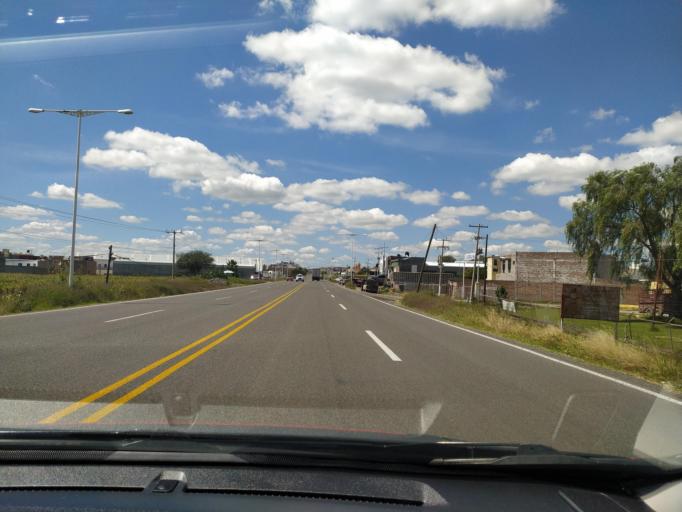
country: MX
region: Jalisco
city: San Miguel el Alto
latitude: 21.0285
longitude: -102.3847
